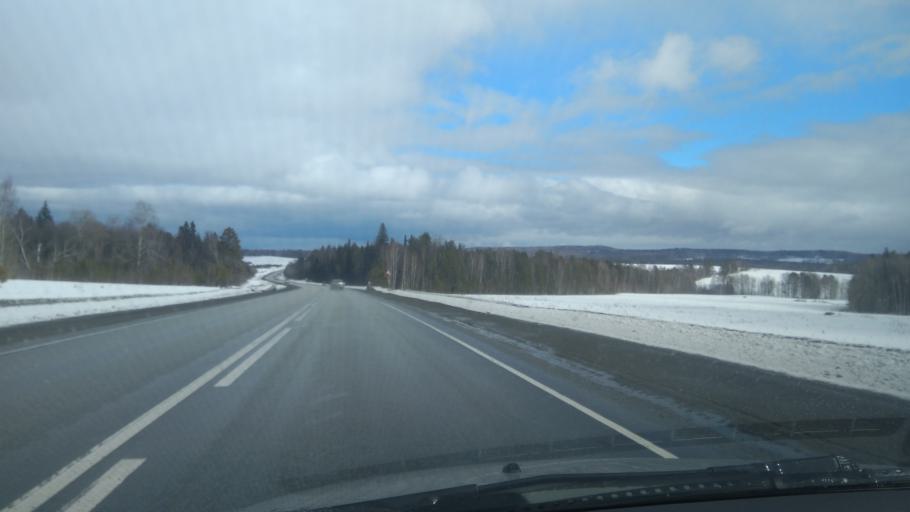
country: RU
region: Sverdlovsk
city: Bisert'
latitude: 56.8005
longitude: 58.7062
